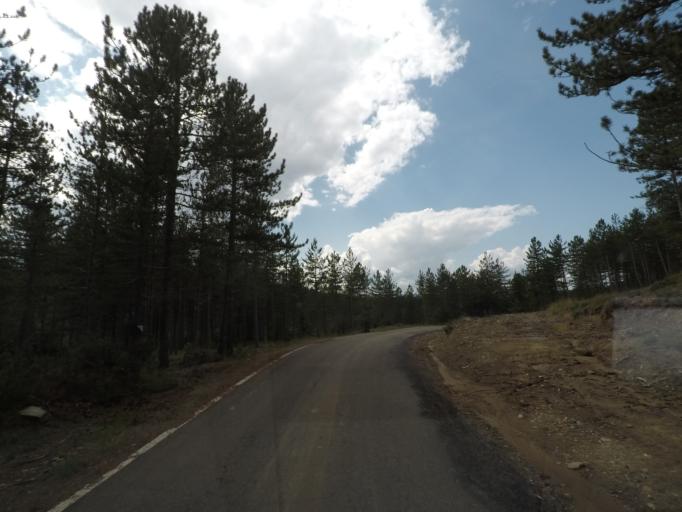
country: ES
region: Aragon
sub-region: Provincia de Huesca
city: Fiscal
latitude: 42.4084
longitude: -0.1558
